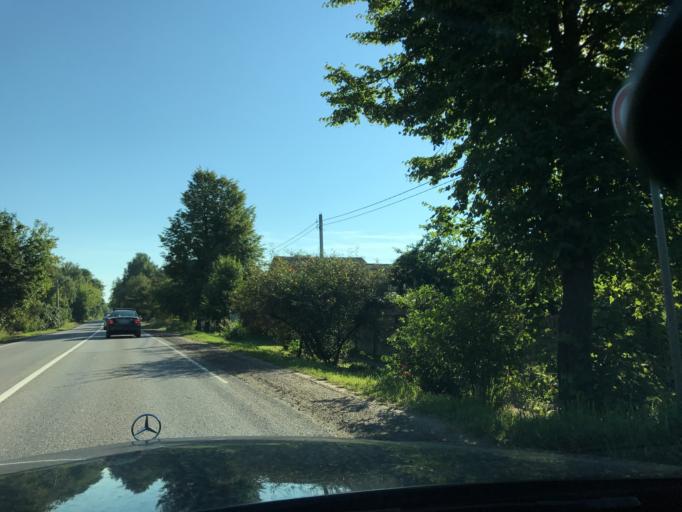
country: RU
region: Moskovskaya
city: Bakhchivandzhi
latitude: 55.8566
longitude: 38.1318
